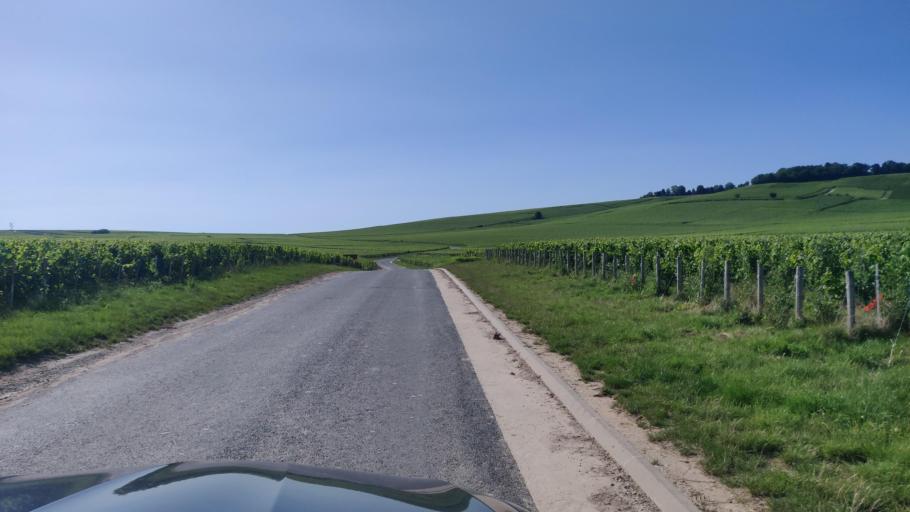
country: FR
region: Champagne-Ardenne
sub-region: Departement de la Marne
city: Tours-sur-Marne
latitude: 49.0866
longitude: 4.1344
